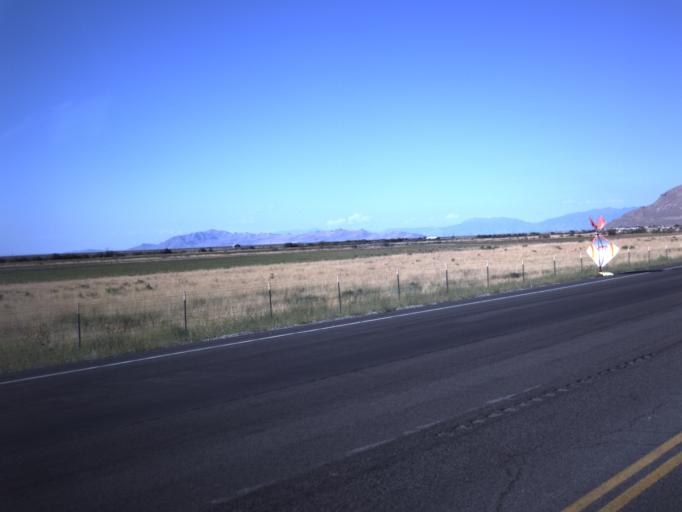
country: US
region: Utah
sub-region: Tooele County
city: Stansbury park
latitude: 40.6377
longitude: -112.3246
